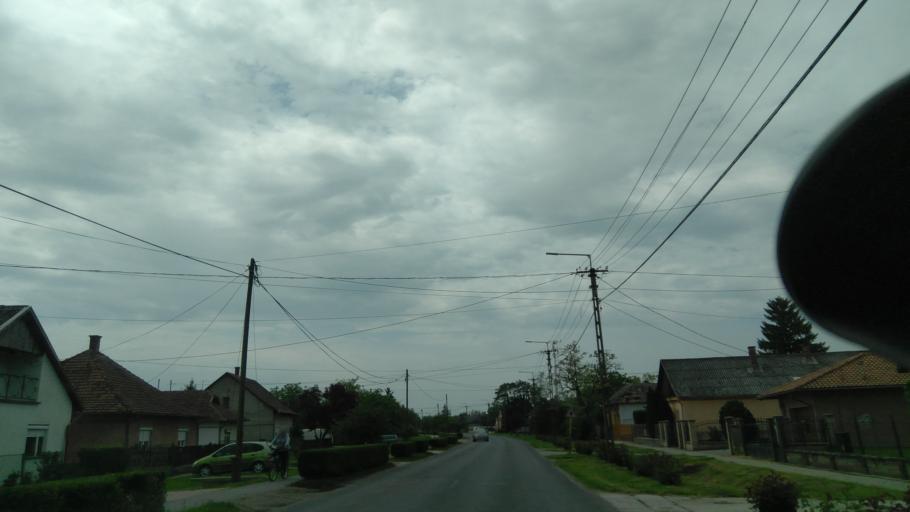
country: HU
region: Bekes
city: Fuzesgyarmat
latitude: 47.1040
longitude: 21.2091
